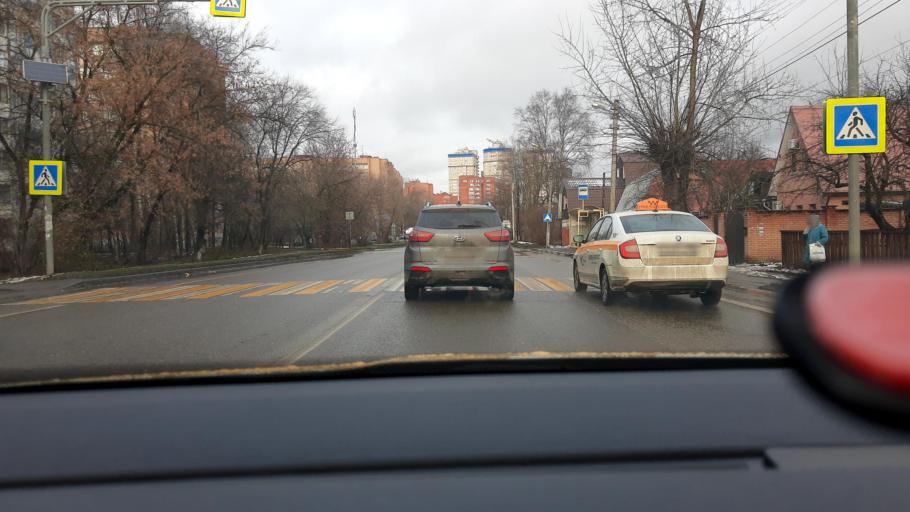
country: RU
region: Moskovskaya
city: Pushkino
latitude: 55.9935
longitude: 37.8674
